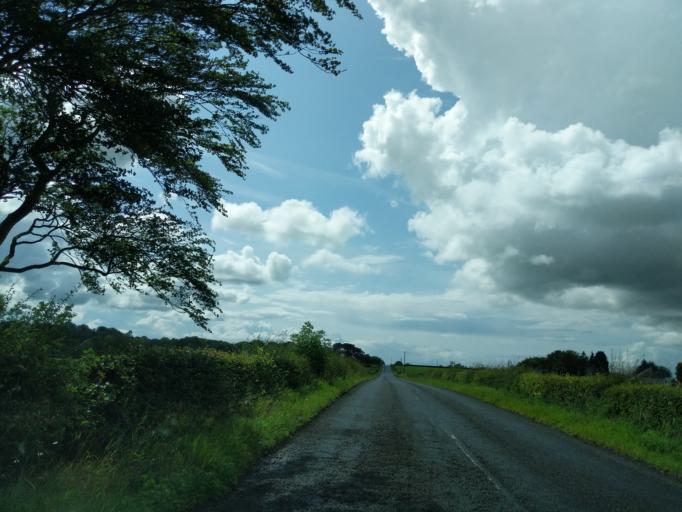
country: GB
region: Scotland
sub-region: East Ayrshire
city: Stewarton
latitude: 55.7189
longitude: -4.5003
